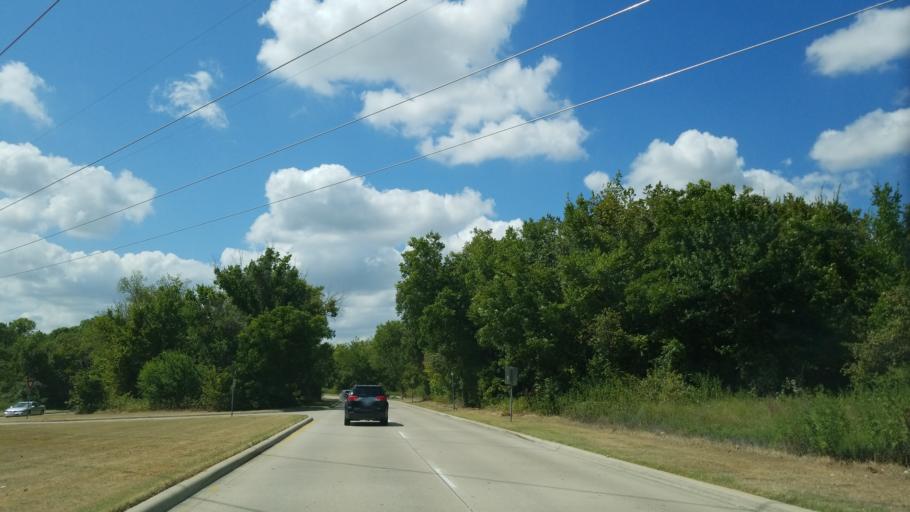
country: US
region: Texas
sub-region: Tarrant County
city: Grapevine
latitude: 32.9222
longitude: -97.0959
